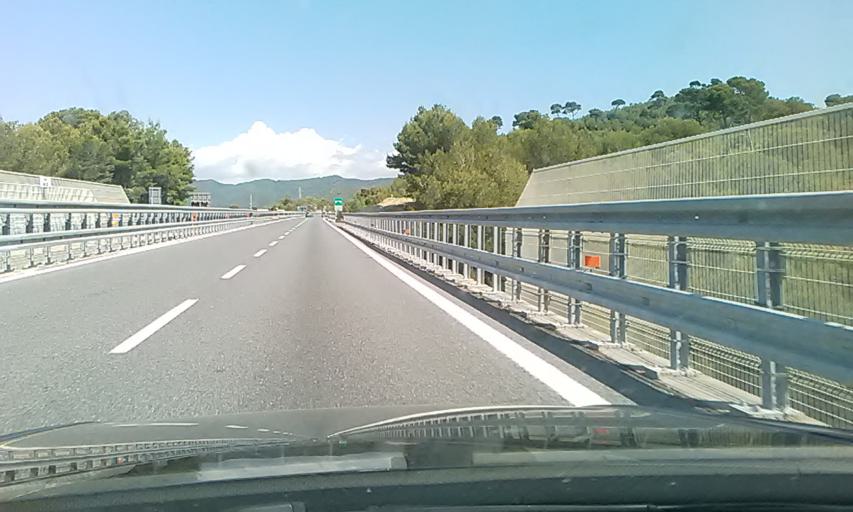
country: IT
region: Liguria
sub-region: Provincia di Savona
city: Laigueglia
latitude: 43.9806
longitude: 8.1388
